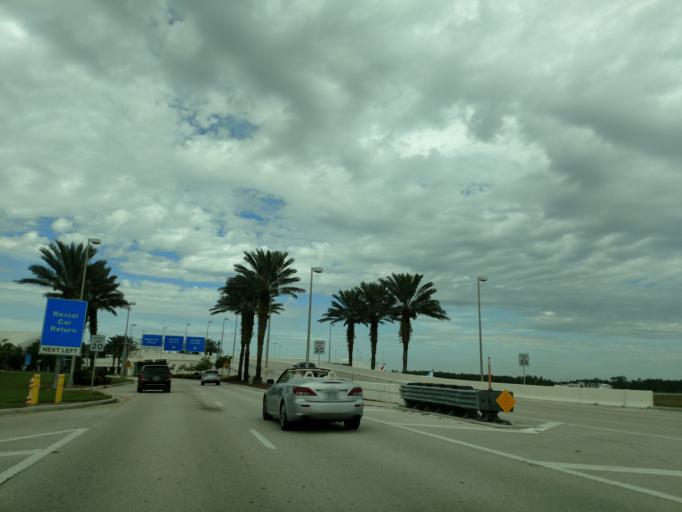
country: US
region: Florida
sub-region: Lee County
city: Gateway
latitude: 26.5247
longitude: -81.7524
